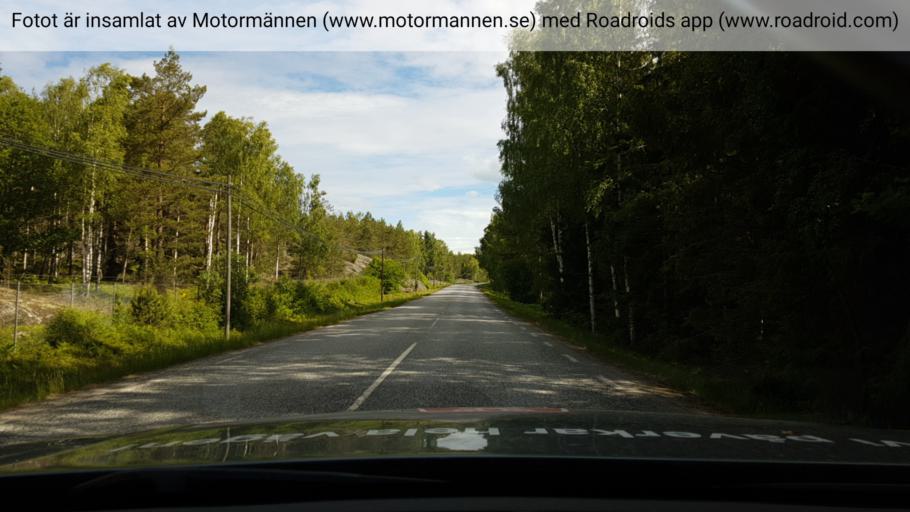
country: SE
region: Stockholm
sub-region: Nynashamns Kommun
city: Nynashamn
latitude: 58.9815
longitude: 18.0898
